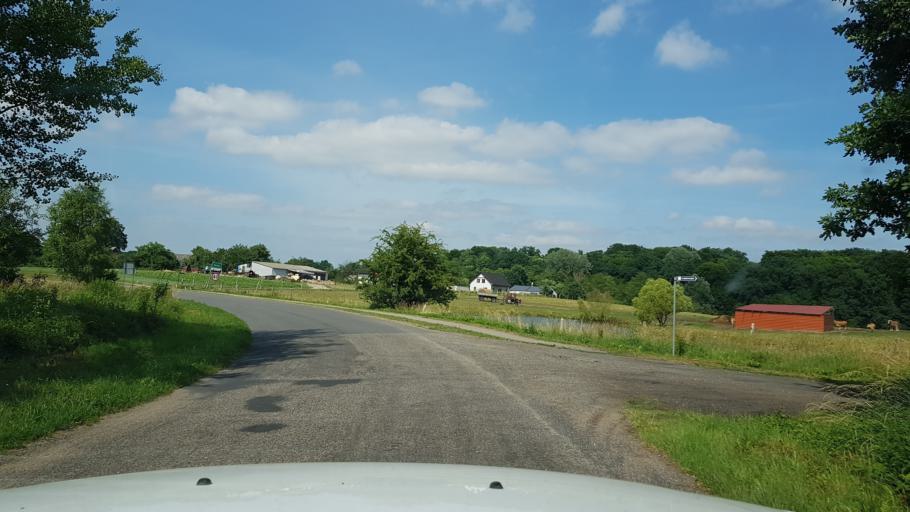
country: PL
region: West Pomeranian Voivodeship
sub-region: Powiat goleniowski
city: Osina
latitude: 53.5998
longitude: 15.0045
